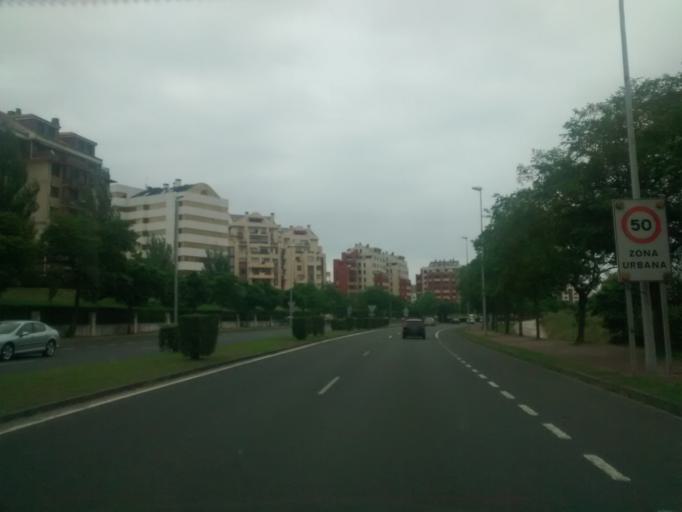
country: ES
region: Cantabria
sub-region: Provincia de Cantabria
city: Santander
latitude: 43.4689
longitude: -3.8240
